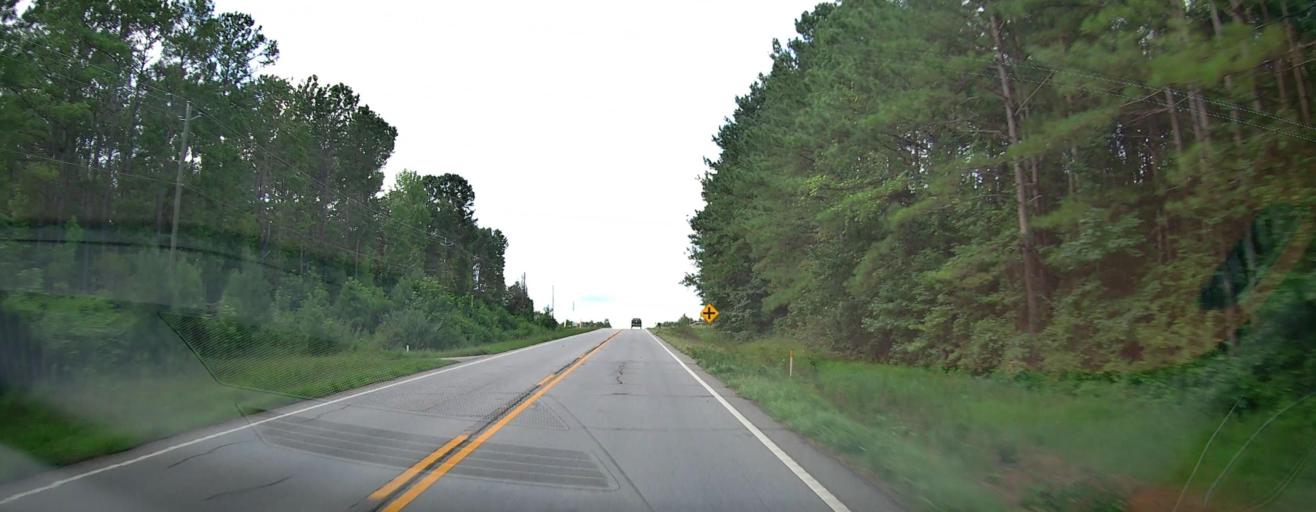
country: US
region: Georgia
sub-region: Meriwether County
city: Greenville
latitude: 33.0343
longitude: -84.5641
